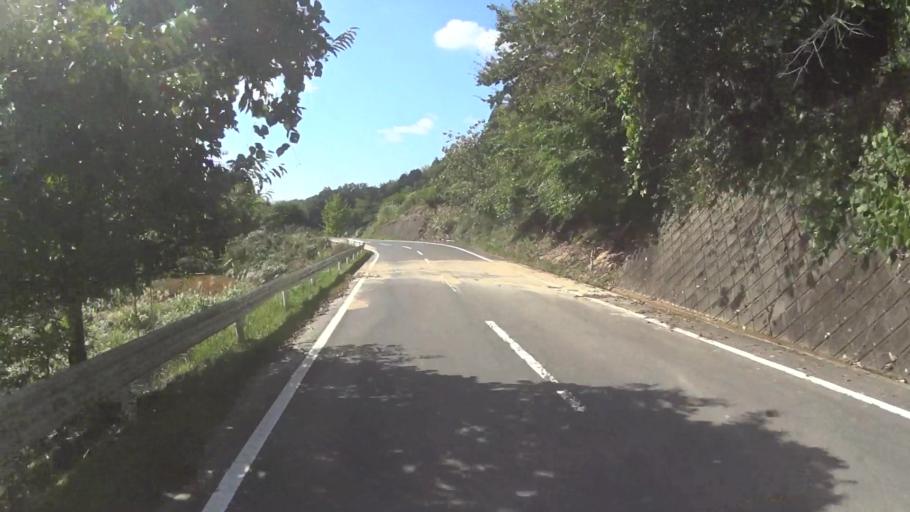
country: JP
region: Hyogo
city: Toyooka
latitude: 35.6078
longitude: 134.9896
